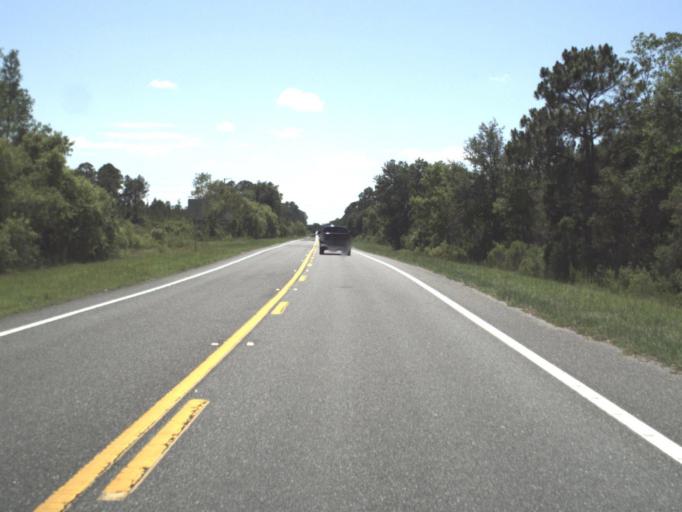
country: US
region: Florida
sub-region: Lafayette County
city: Mayo
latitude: 30.1292
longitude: -83.3651
